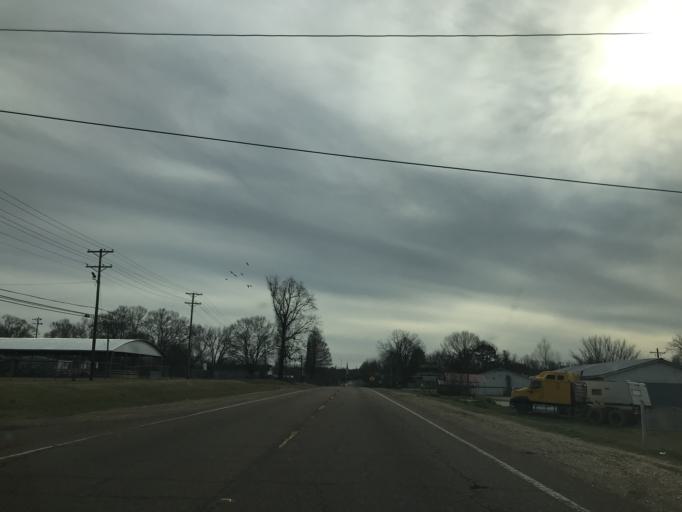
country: US
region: Mississippi
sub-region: Claiborne County
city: Port Gibson
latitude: 31.9717
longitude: -90.9780
